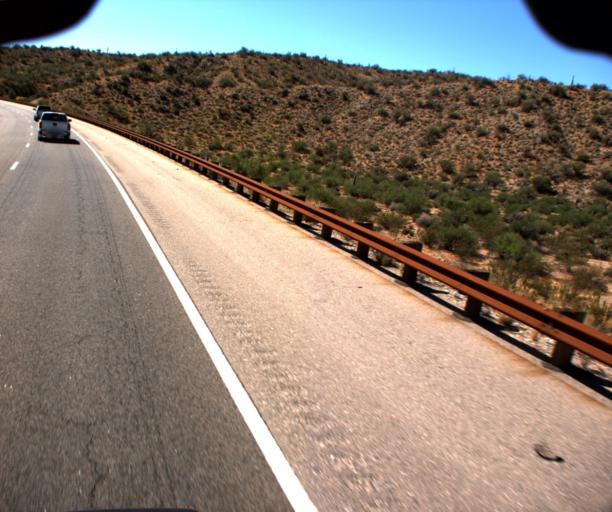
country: US
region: Arizona
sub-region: Yavapai County
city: Bagdad
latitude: 34.3907
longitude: -113.2087
